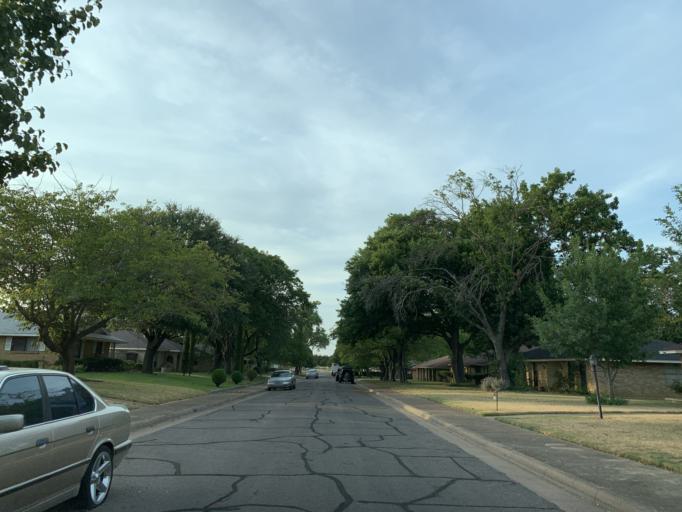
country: US
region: Texas
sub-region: Dallas County
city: Cockrell Hill
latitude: 32.6949
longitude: -96.8861
